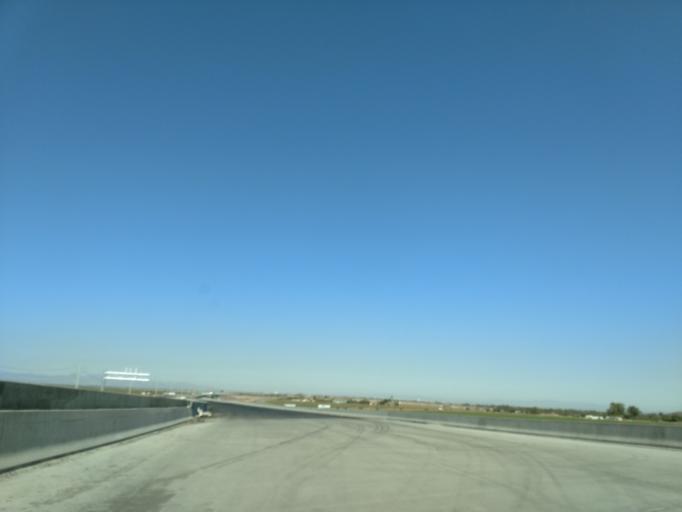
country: US
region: Arizona
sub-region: Maricopa County
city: Laveen
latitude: 33.3244
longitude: -112.1659
